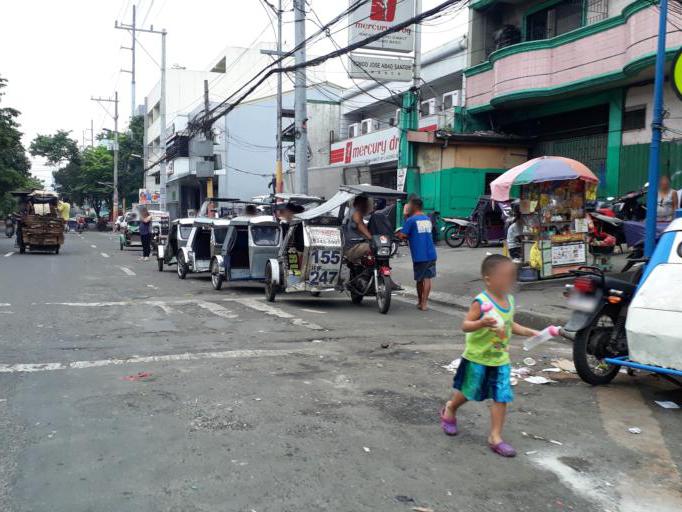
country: PH
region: Metro Manila
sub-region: City of Manila
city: Manila
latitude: 14.6258
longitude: 120.9785
